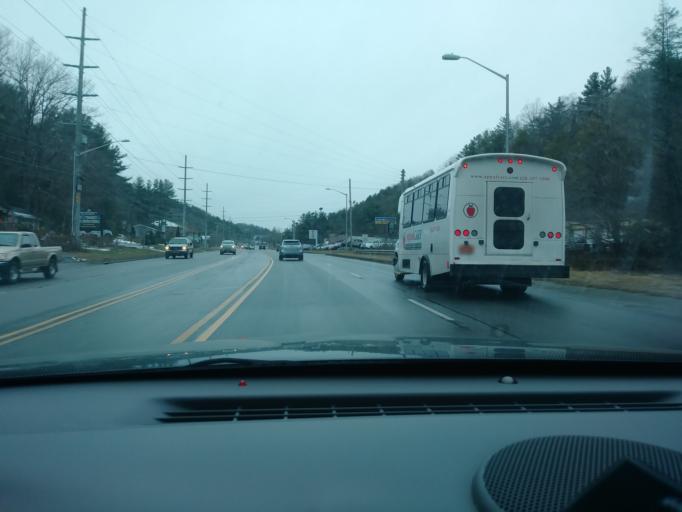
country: US
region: North Carolina
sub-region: Watauga County
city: Boone
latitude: 36.2040
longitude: -81.6901
